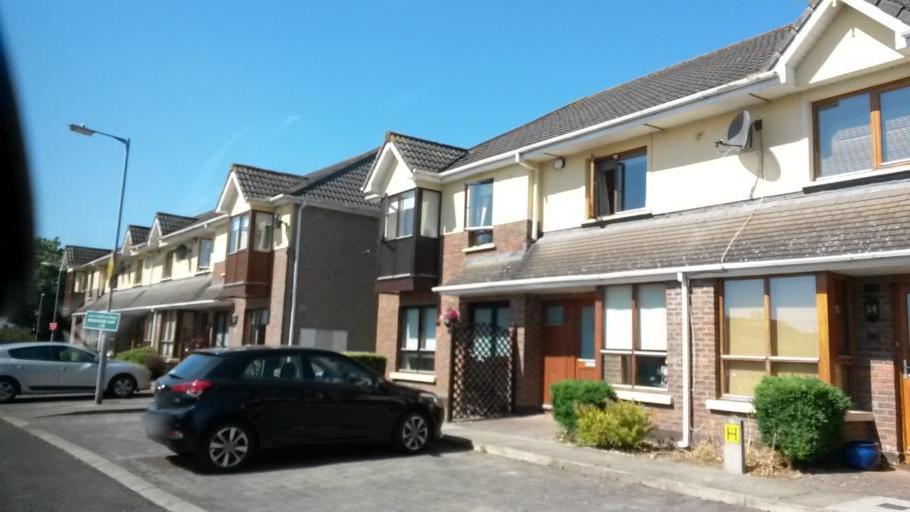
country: IE
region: Leinster
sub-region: Fingal County
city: Swords
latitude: 53.4466
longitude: -6.2501
